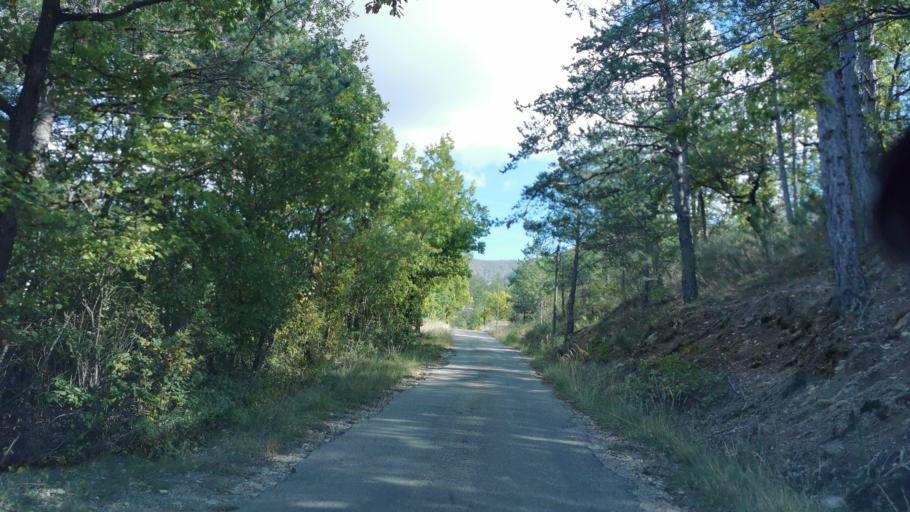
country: FR
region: Provence-Alpes-Cote d'Azur
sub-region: Departement des Alpes-de-Haute-Provence
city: Volonne
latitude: 44.1839
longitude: 6.0241
